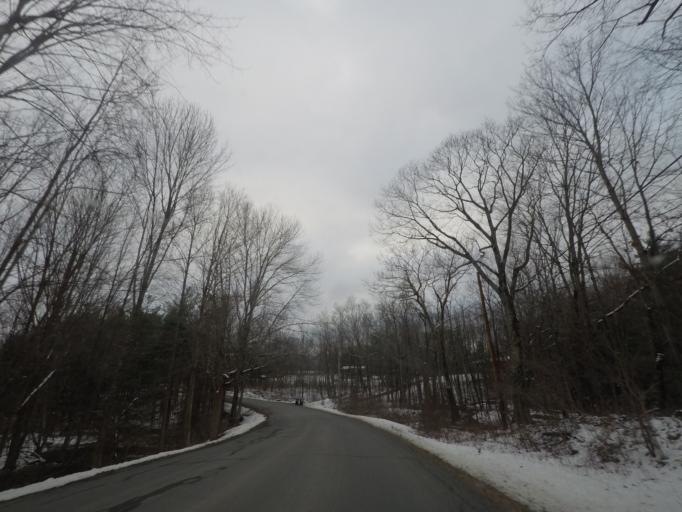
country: US
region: New York
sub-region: Rensselaer County
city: Averill Park
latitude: 42.6434
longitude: -73.5383
